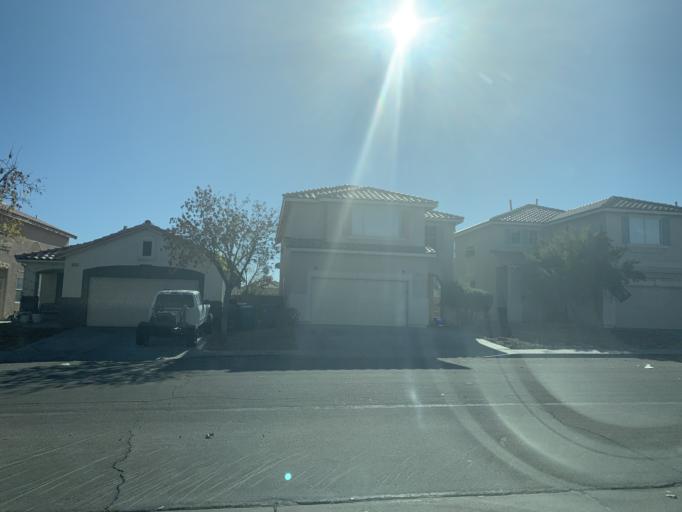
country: US
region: Nevada
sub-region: Clark County
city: Summerlin South
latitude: 36.1251
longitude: -115.3005
